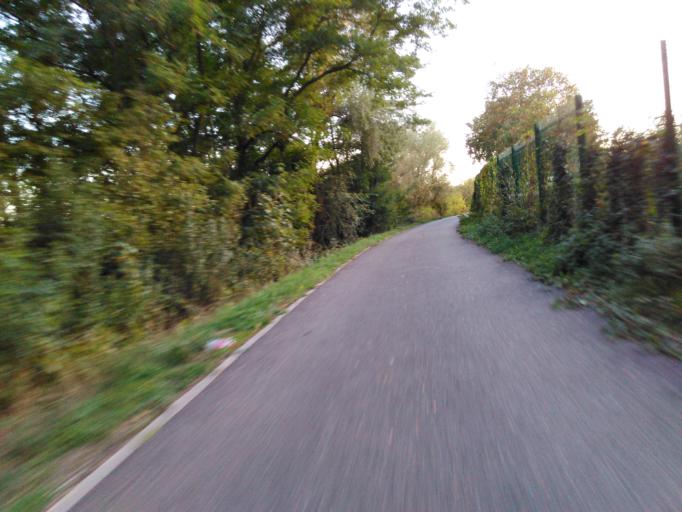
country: FR
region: Lorraine
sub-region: Departement de la Moselle
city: Saint-Julien-les-Metz
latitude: 49.1412
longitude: 6.1956
